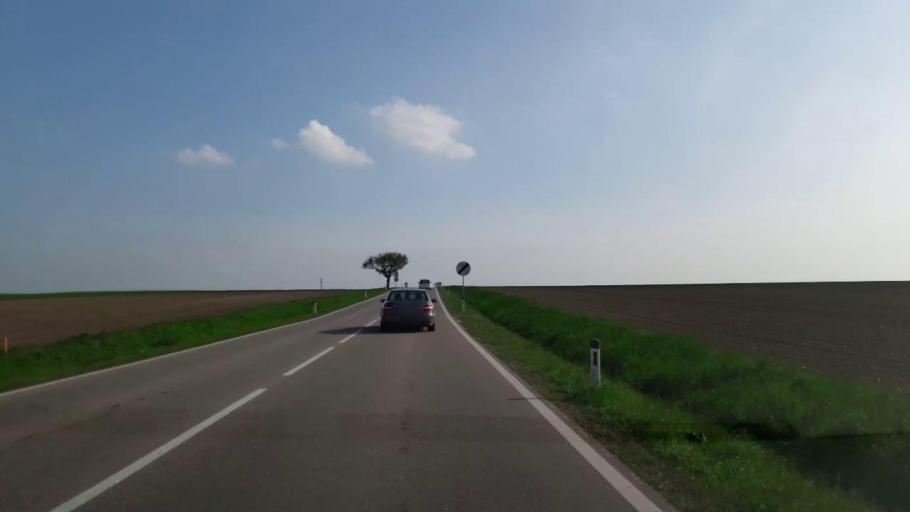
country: AT
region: Lower Austria
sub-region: Politischer Bezirk Hollabrunn
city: Wullersdorf
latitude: 48.6155
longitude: 16.0674
